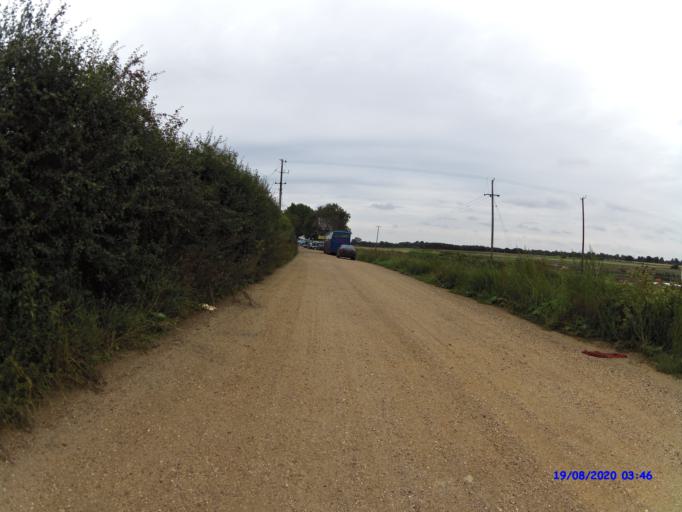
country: GB
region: England
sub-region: Cambridgeshire
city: Ramsey
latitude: 52.4590
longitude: -0.1103
